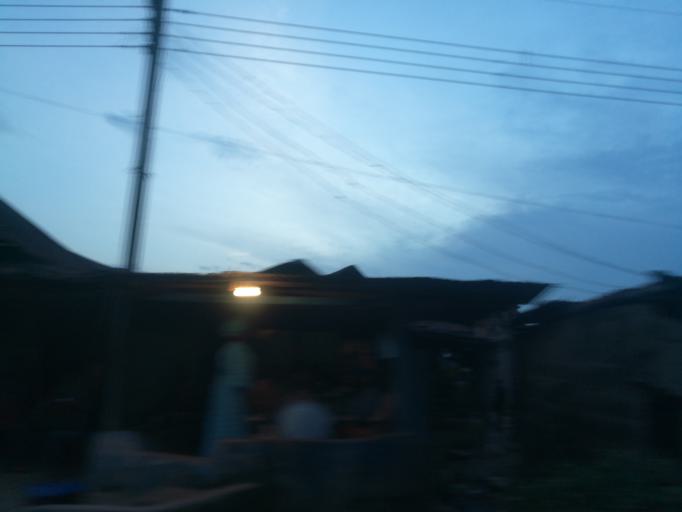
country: NG
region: Oyo
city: Ibadan
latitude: 7.3745
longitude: 3.9016
